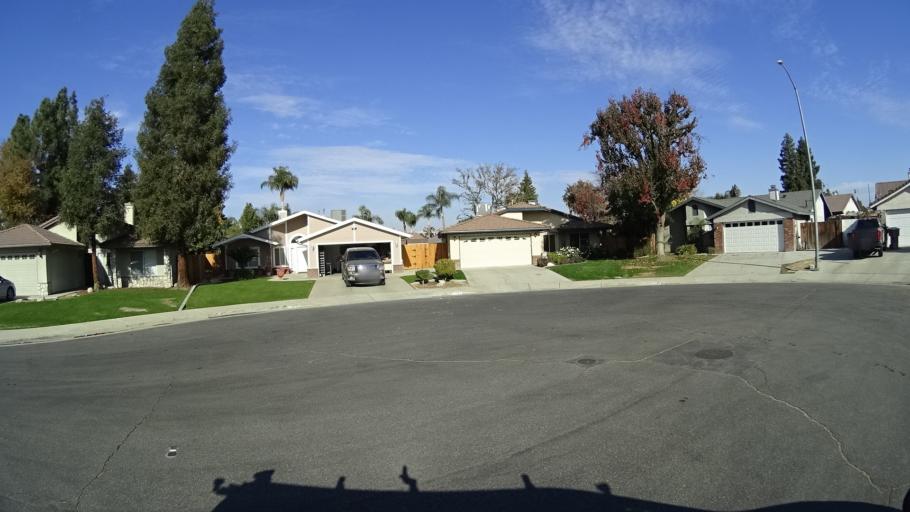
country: US
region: California
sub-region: Kern County
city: Greenacres
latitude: 35.3982
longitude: -119.0869
